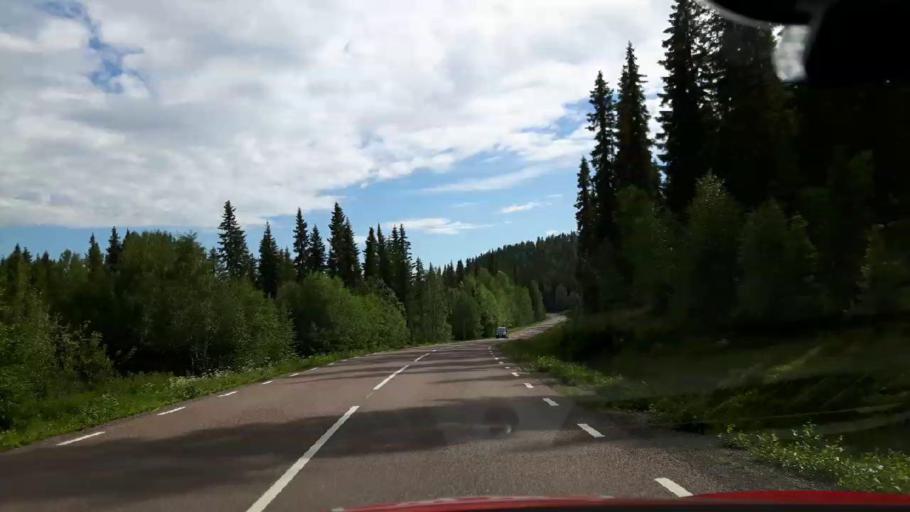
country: SE
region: Jaemtland
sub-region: Krokoms Kommun
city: Valla
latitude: 63.9218
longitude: 14.2146
